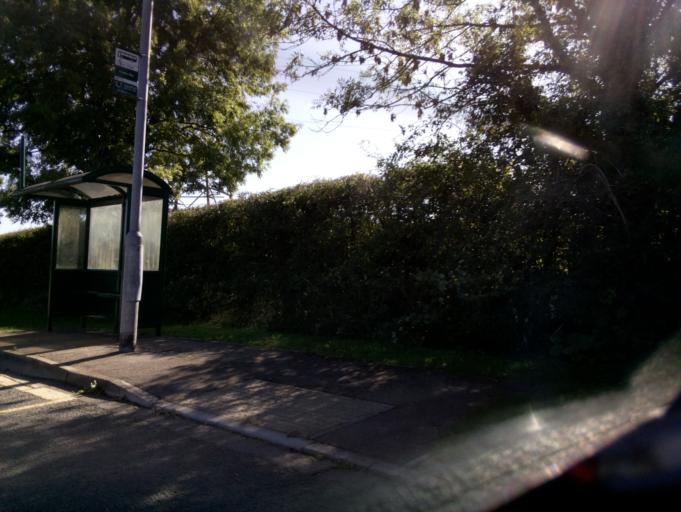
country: GB
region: Wales
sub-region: Torfaen County Borough
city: Cwmbran
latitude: 51.6345
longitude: -3.0583
